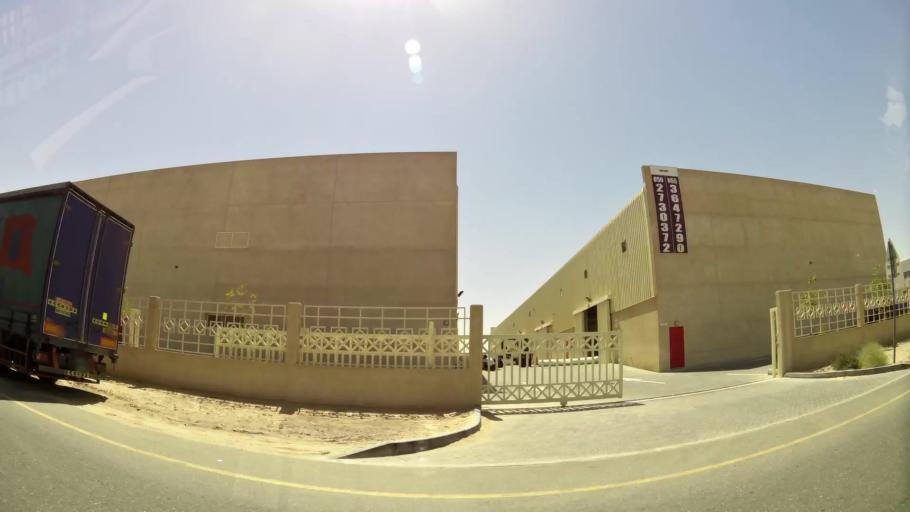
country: AE
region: Dubai
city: Dubai
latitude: 24.9758
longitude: 55.2092
